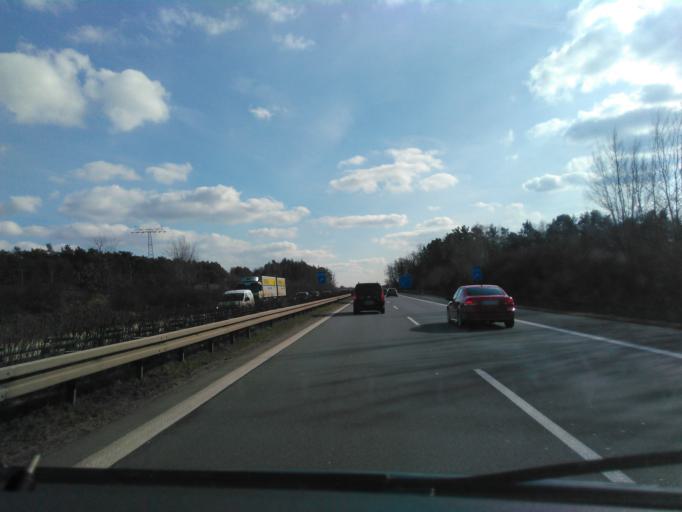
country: DE
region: Brandenburg
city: Mittenwalde
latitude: 52.2718
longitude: 13.5726
